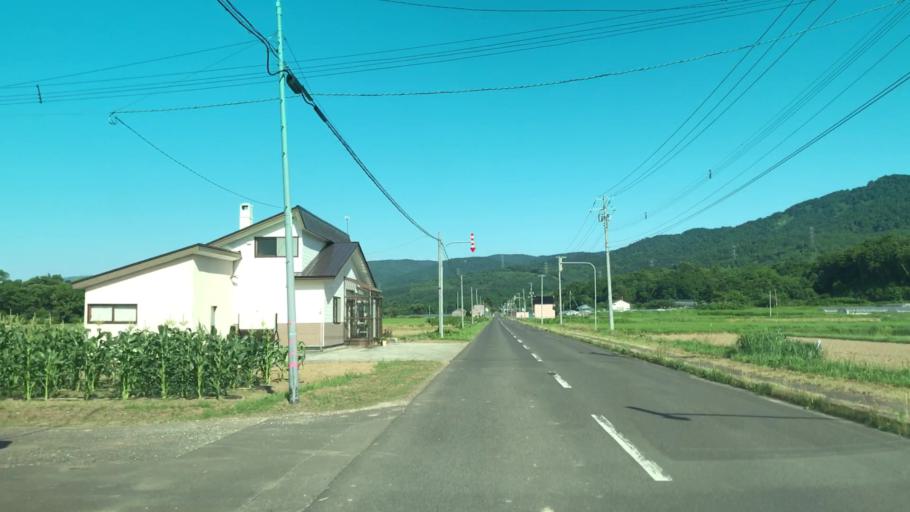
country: JP
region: Hokkaido
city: Yoichi
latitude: 43.0368
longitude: 140.7453
